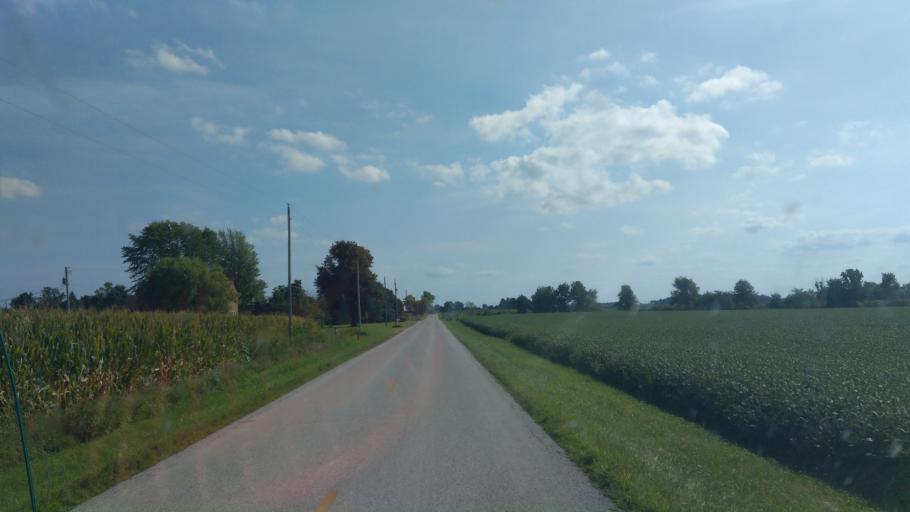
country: US
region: Ohio
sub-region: Hardin County
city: Forest
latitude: 40.6976
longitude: -83.5144
